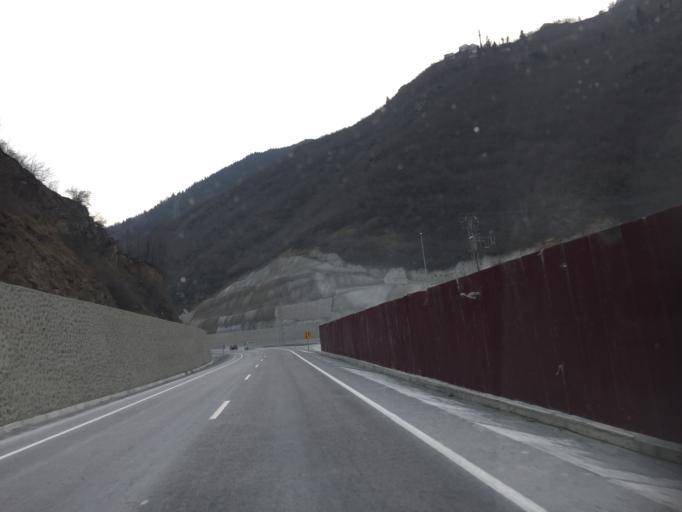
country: TR
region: Trabzon
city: Macka
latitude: 40.7664
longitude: 39.5645
